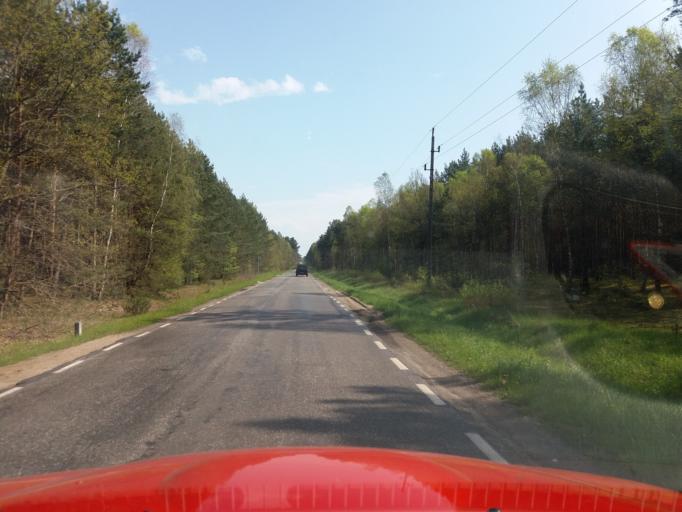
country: PL
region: West Pomeranian Voivodeship
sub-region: Powiat drawski
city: Kalisz Pomorski
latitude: 53.2664
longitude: 15.8669
